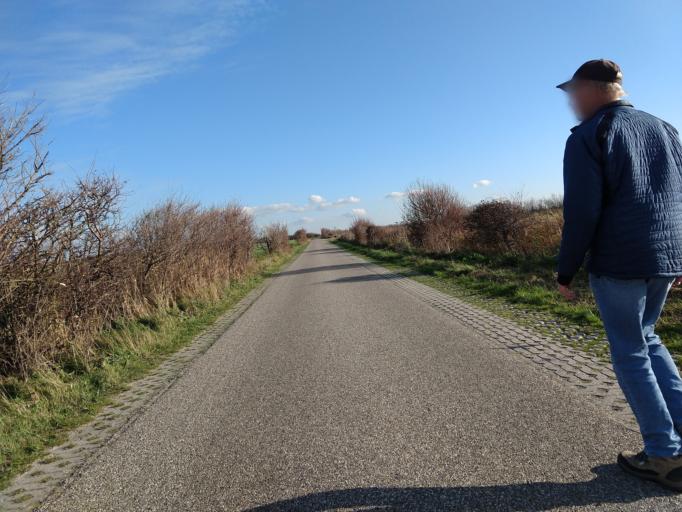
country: NL
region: Zeeland
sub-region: Gemeente Vlissingen
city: Vlissingen
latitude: 51.5473
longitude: 3.4619
